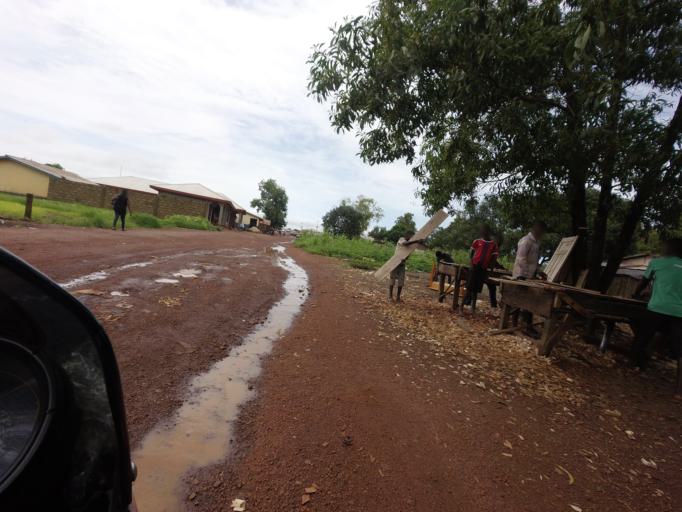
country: SL
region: Northern Province
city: Kambia
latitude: 9.1061
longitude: -12.9257
